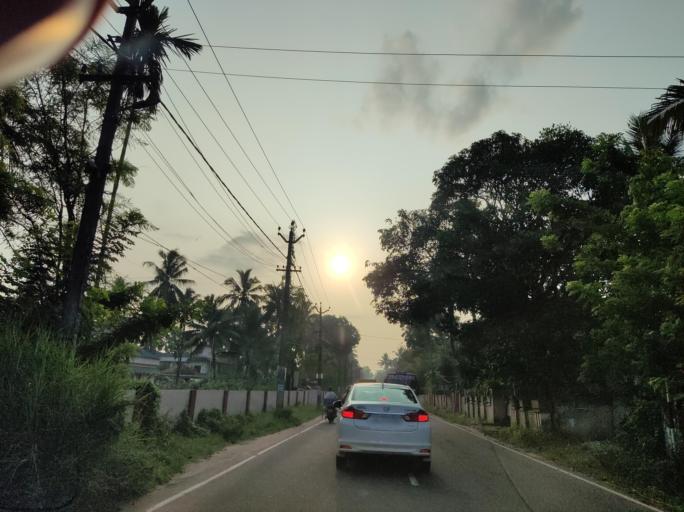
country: IN
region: Kerala
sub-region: Alappuzha
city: Kayankulam
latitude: 9.1762
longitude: 76.5170
